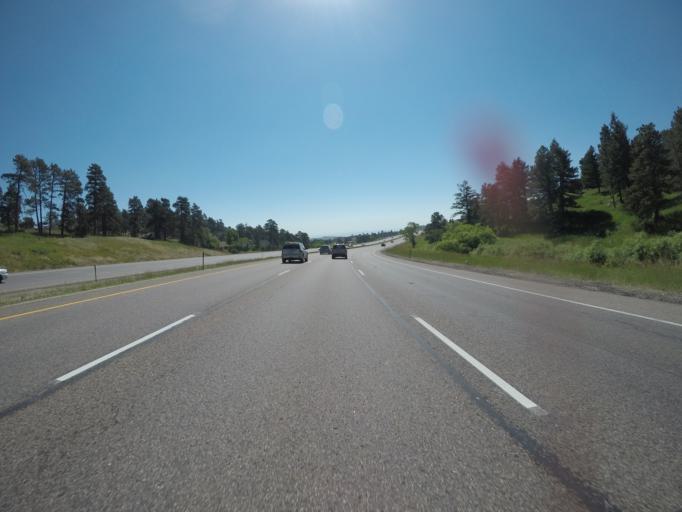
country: US
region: Colorado
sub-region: Jefferson County
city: Genesee
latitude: 39.7089
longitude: -105.2843
